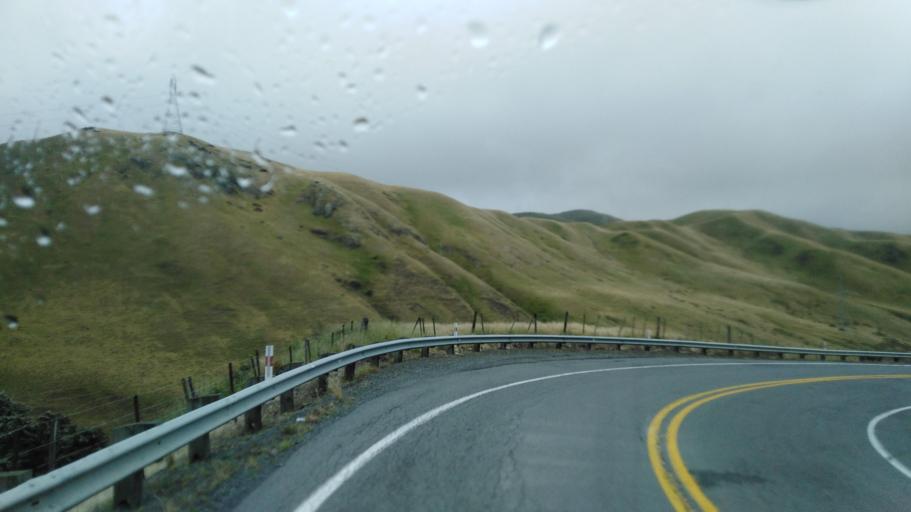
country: NZ
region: Marlborough
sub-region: Marlborough District
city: Blenheim
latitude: -41.5809
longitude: 174.0405
